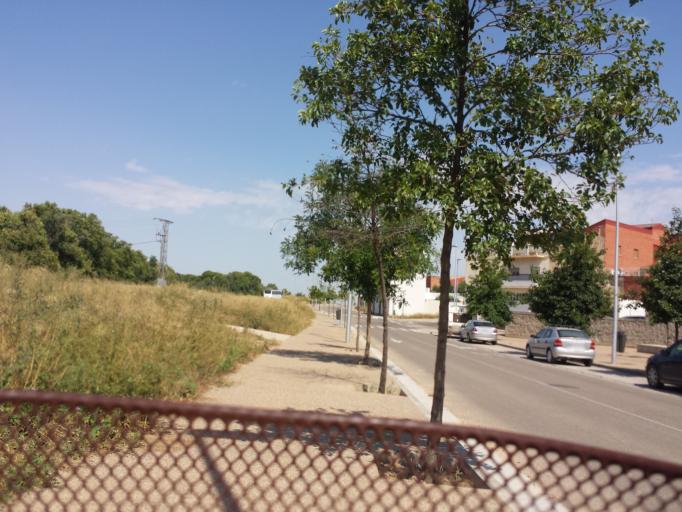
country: ES
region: Aragon
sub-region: Provincia de Zaragoza
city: Montecanal
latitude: 41.6362
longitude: -0.9350
